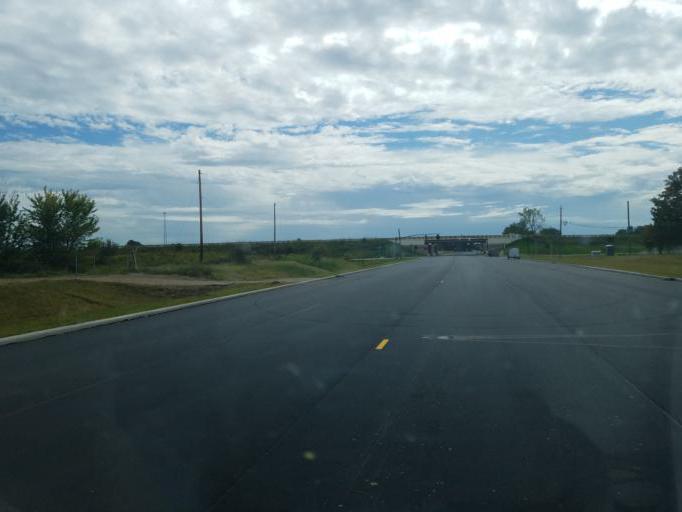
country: US
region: Ohio
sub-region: Licking County
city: Johnstown
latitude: 40.0826
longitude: -82.7210
